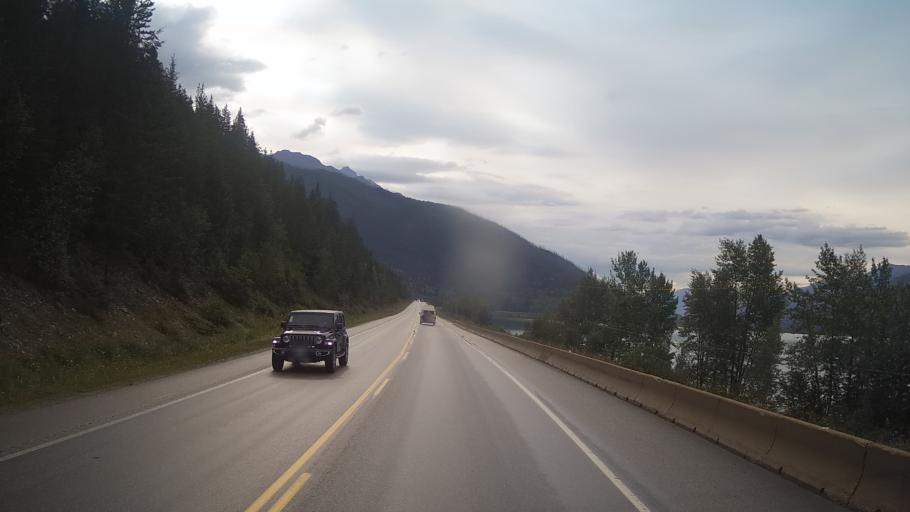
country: CA
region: Alberta
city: Jasper Park Lodge
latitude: 52.9561
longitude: -118.8927
